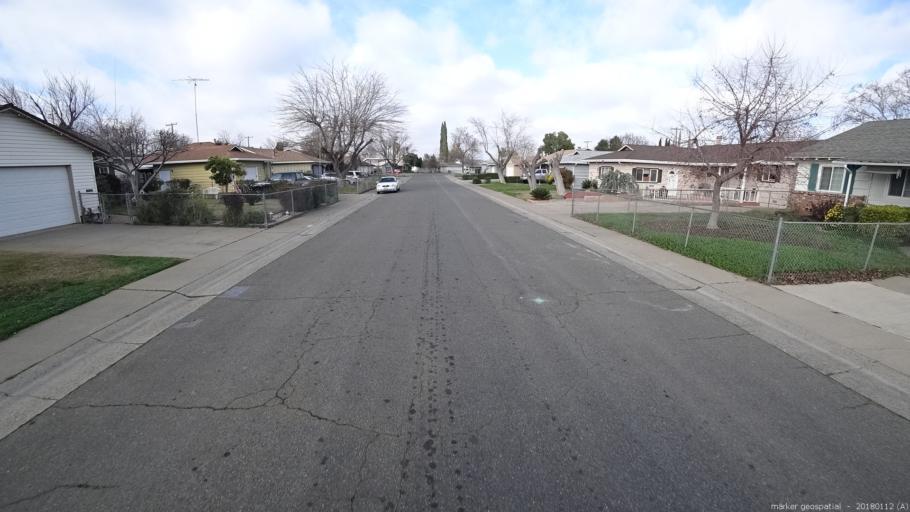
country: US
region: California
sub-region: Sacramento County
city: Rancho Cordova
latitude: 38.5938
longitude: -121.3033
